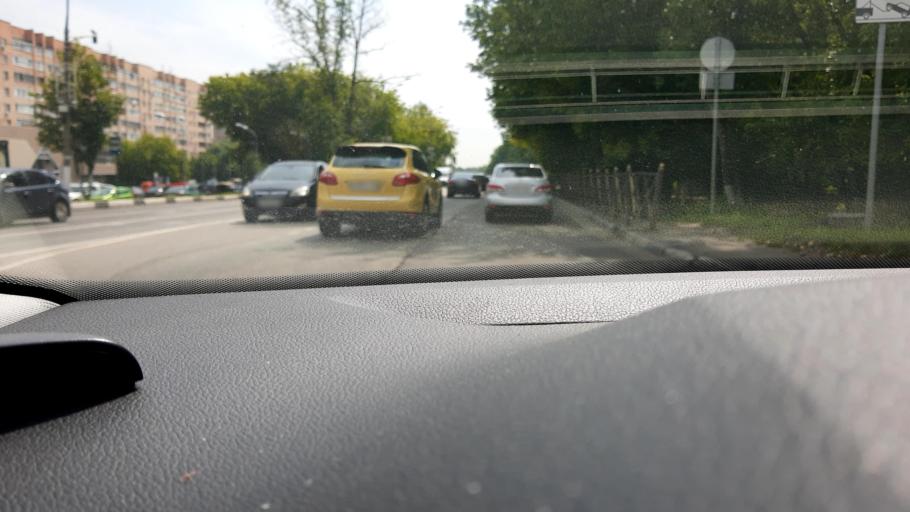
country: RU
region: Moskovskaya
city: Krasnogorsk
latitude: 55.8288
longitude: 37.3069
